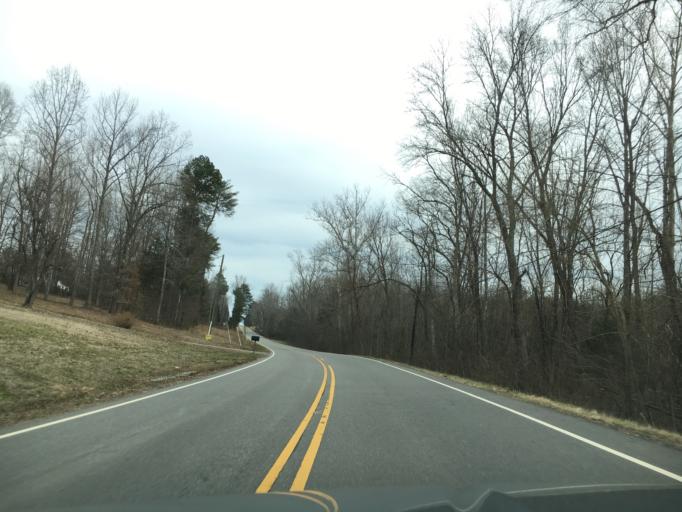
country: US
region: Virginia
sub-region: Charlotte County
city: Charlotte Court House
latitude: 37.0756
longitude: -78.7356
